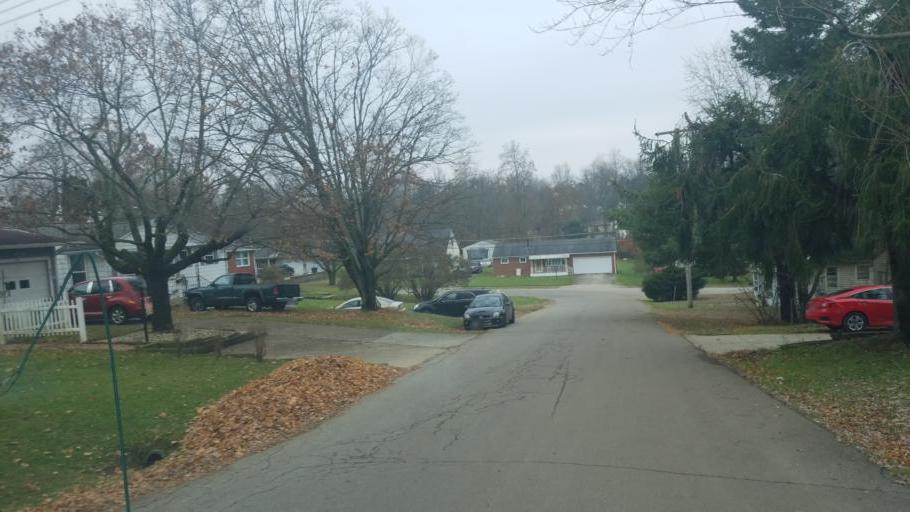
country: US
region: Ohio
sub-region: Richland County
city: Mansfield
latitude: 40.7406
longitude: -82.5052
